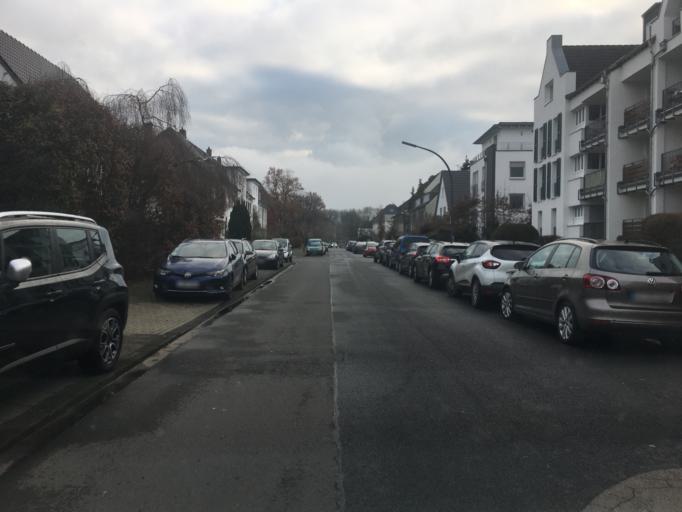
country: DE
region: North Rhine-Westphalia
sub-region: Regierungsbezirk Koln
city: Bayenthal
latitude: 50.9068
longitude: 6.9654
